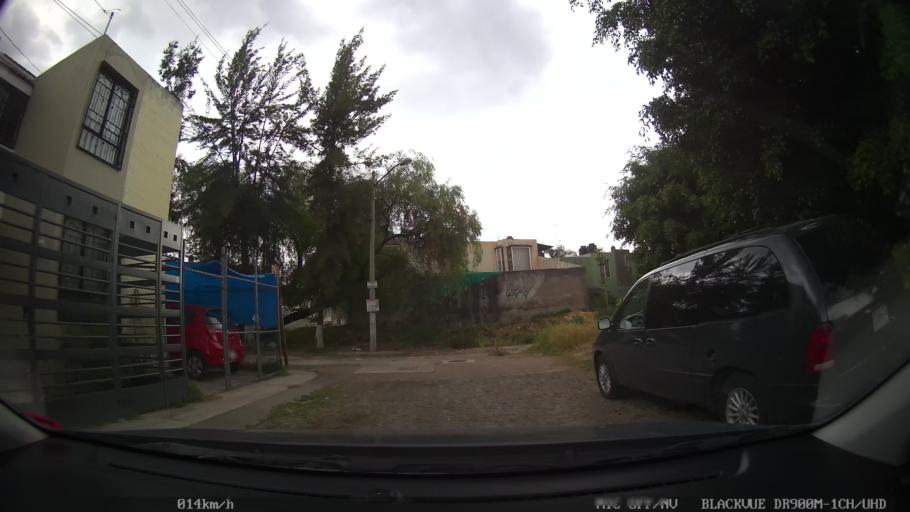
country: MX
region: Jalisco
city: Tlaquepaque
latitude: 20.6254
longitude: -103.2797
